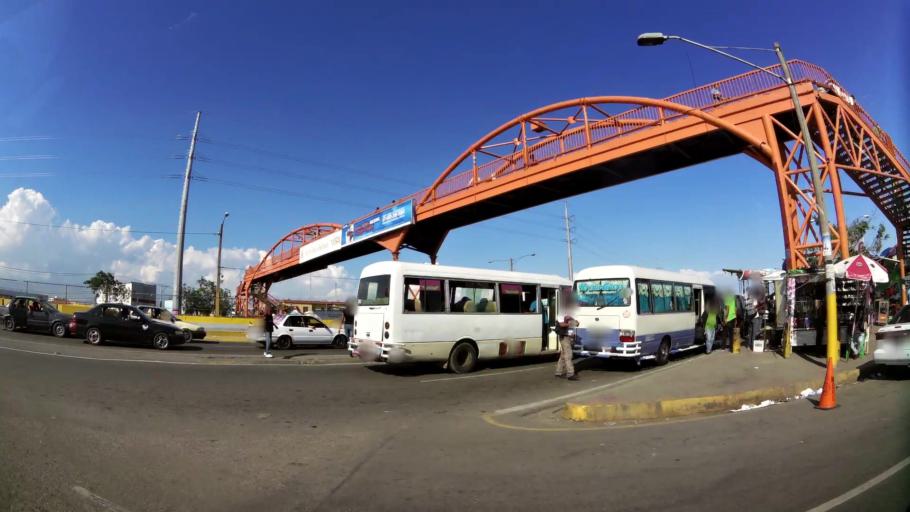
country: DO
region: Nacional
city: Santo Domingo
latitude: 18.4787
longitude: -69.9695
